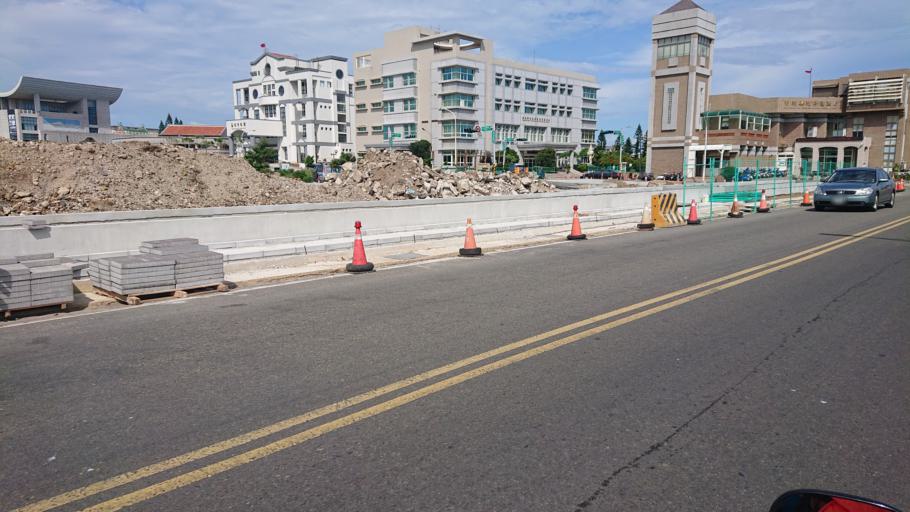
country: TW
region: Taiwan
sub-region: Penghu
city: Ma-kung
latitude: 23.5657
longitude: 119.5773
